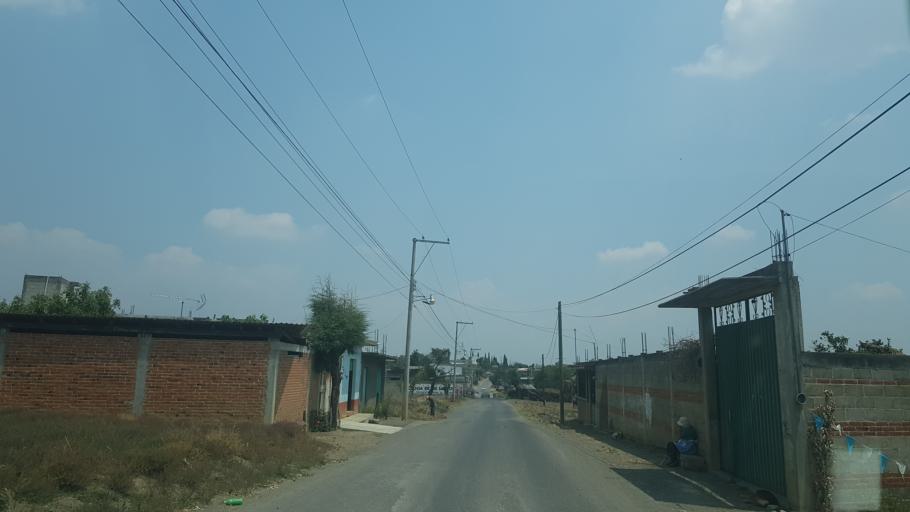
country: MX
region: Puebla
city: San Andres Calpan
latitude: 19.0984
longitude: -98.4768
